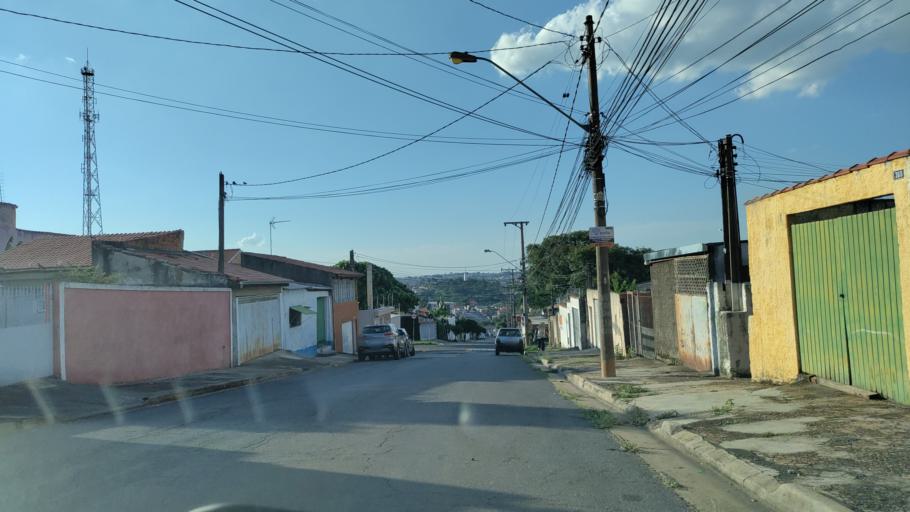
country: BR
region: Sao Paulo
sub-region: Sorocaba
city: Sorocaba
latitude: -23.4756
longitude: -47.4652
